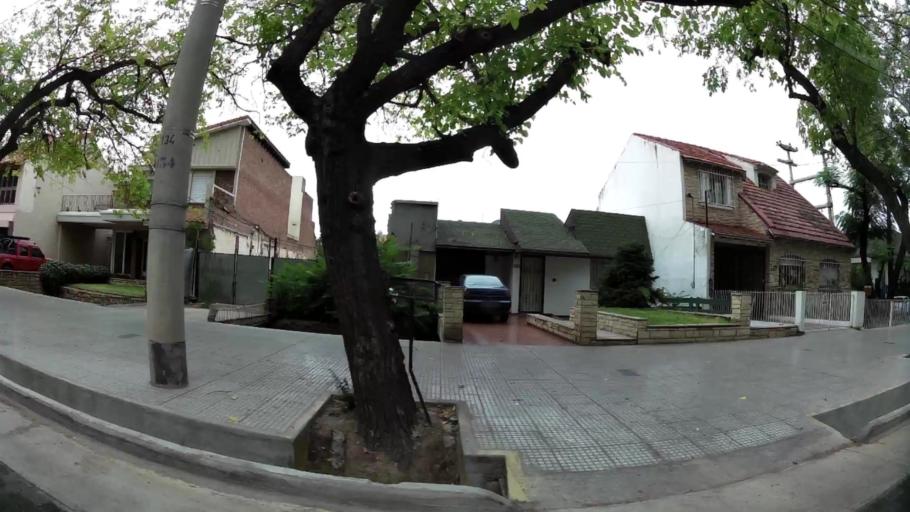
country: AR
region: Mendoza
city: Mendoza
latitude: -32.8830
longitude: -68.8605
